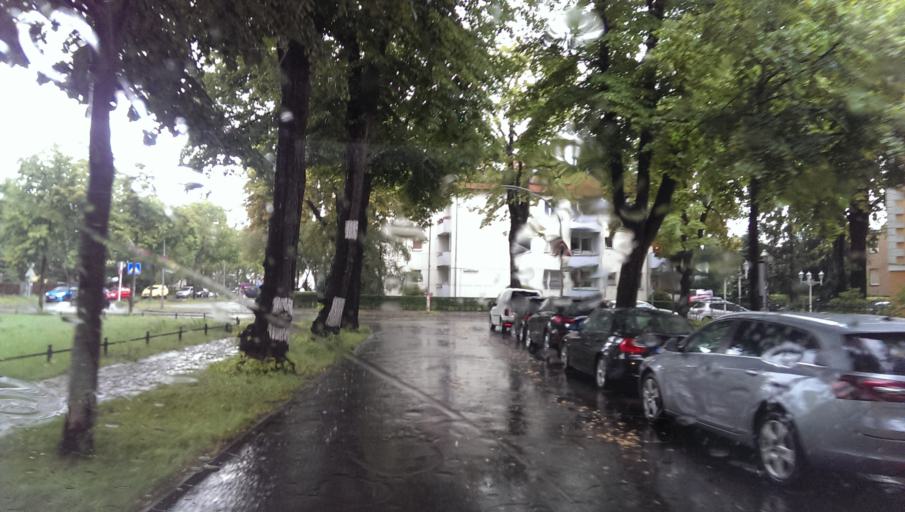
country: DE
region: Berlin
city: Lankwitz
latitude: 52.4253
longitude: 13.3282
